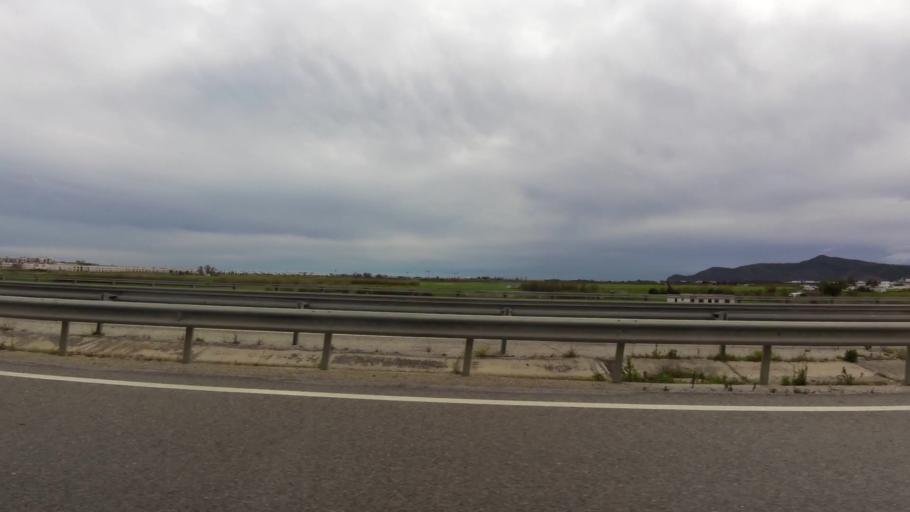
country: MA
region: Tanger-Tetouan
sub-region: Tetouan
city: Martil
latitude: 35.7088
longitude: -5.3559
